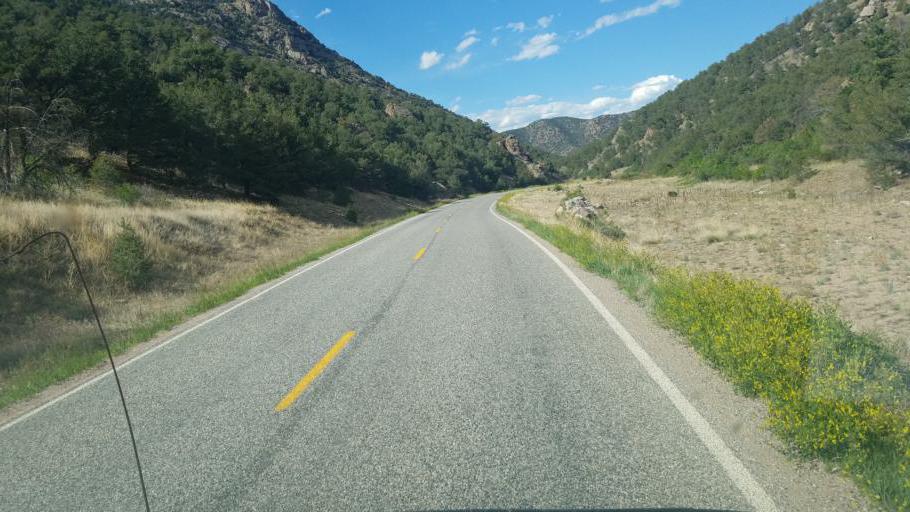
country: US
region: Colorado
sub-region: Fremont County
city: Canon City
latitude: 38.3933
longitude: -105.4488
